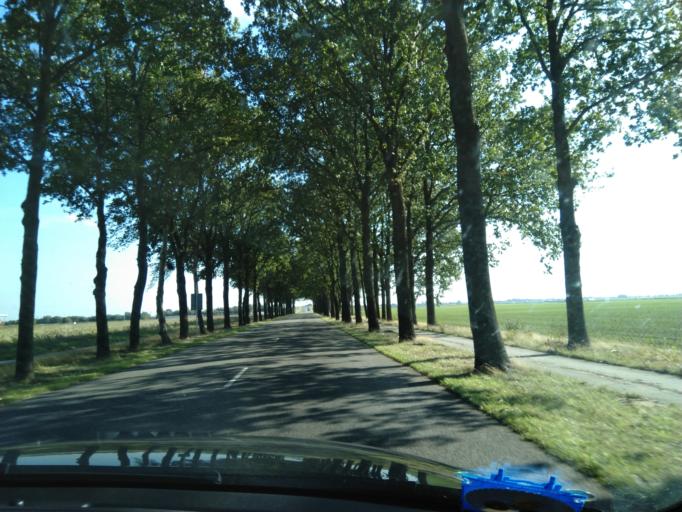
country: NL
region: Groningen
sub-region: Gemeente Veendam
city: Veendam
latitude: 53.0825
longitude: 6.8755
